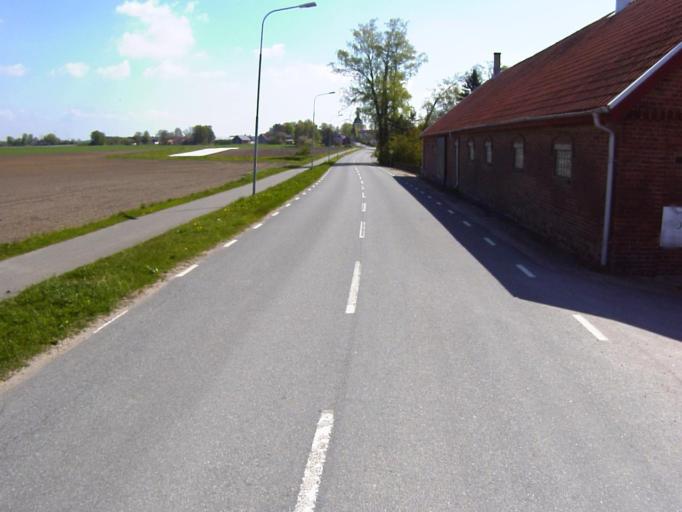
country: SE
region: Skane
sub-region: Kristianstads Kommun
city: Fjalkinge
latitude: 56.0107
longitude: 14.2388
